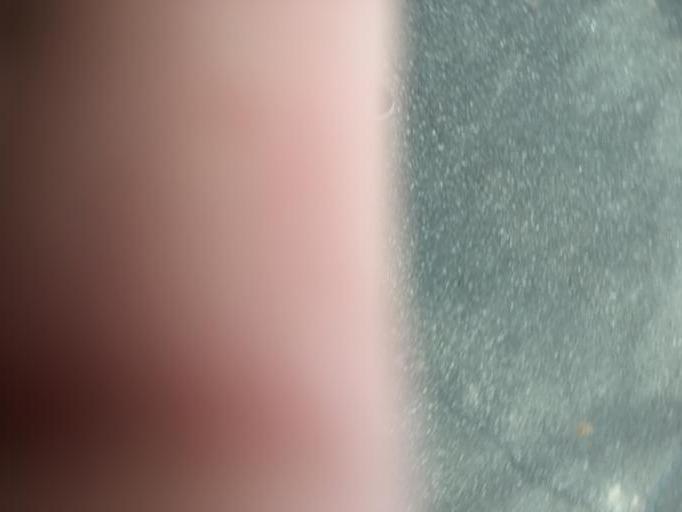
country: US
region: South Carolina
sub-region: Greenville County
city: Greenville
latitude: 34.8479
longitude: -82.3852
